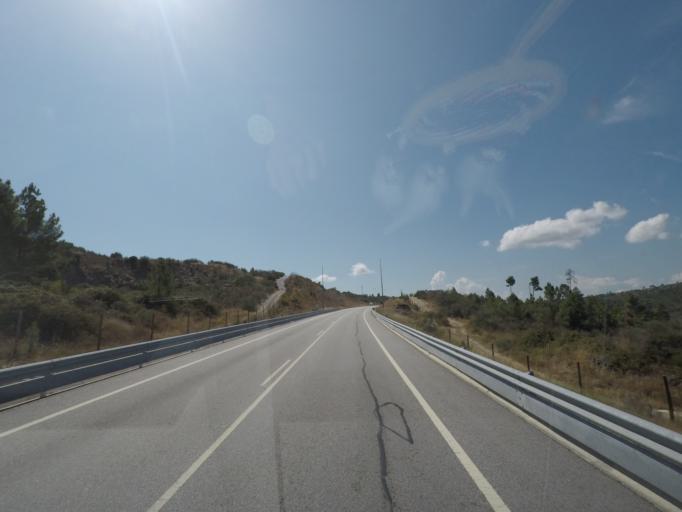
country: PT
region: Braganca
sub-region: Braganca Municipality
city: Vila Flor
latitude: 41.2857
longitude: -7.1930
